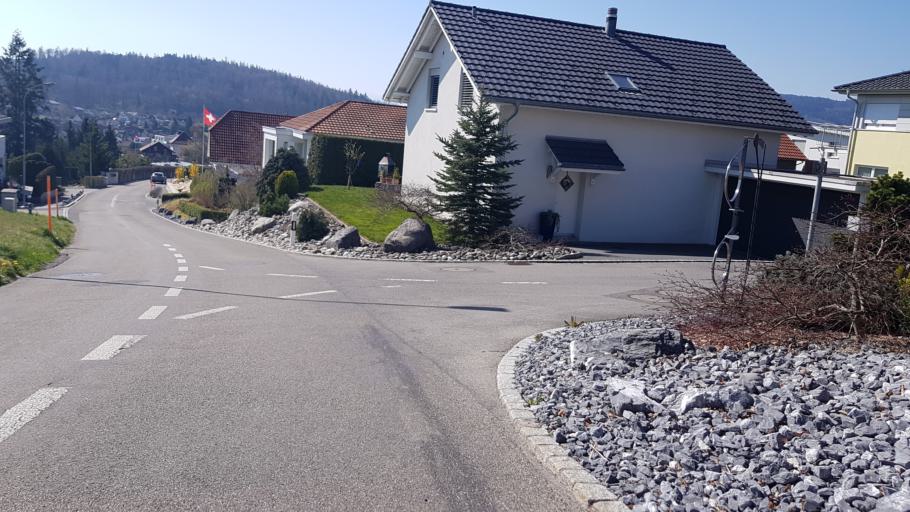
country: CH
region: Aargau
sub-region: Bezirk Kulm
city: Reinach
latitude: 47.2695
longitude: 8.1962
